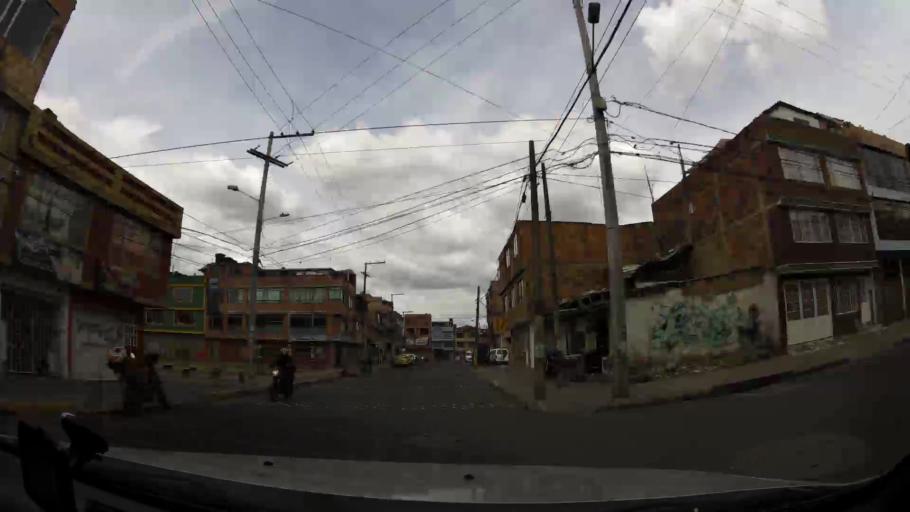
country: CO
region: Cundinamarca
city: Soacha
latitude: 4.6394
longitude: -74.1635
